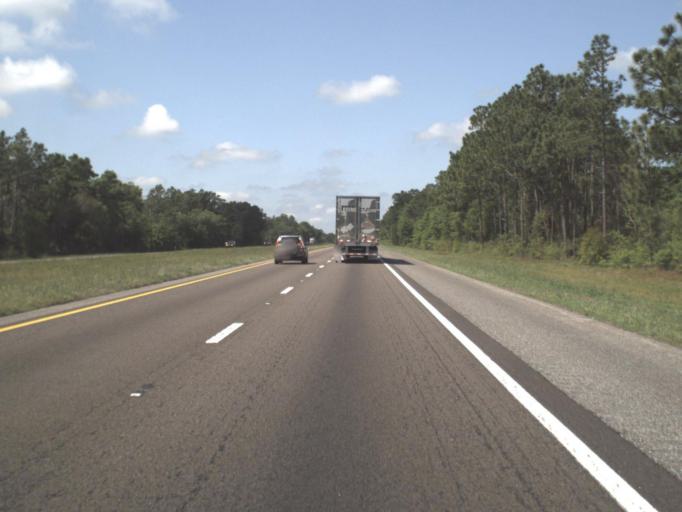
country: US
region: Florida
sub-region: Santa Rosa County
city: East Milton
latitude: 30.6467
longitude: -86.8977
